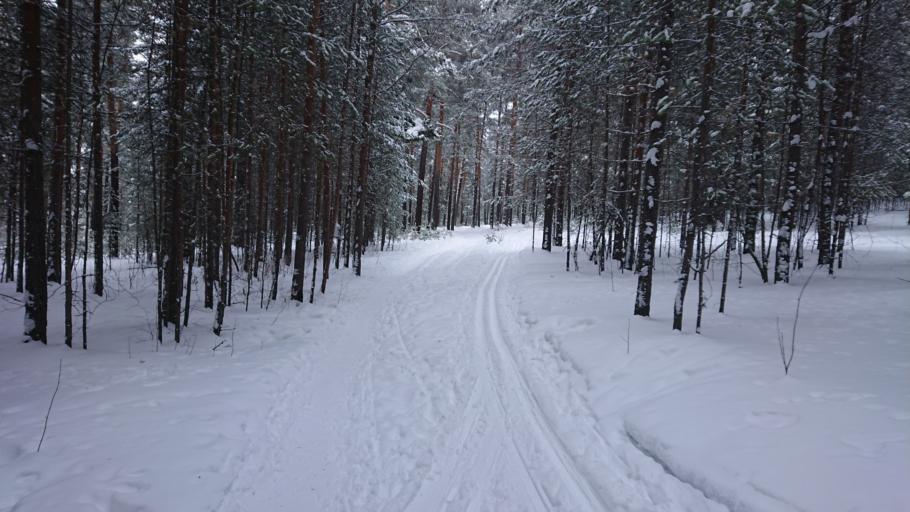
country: RU
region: Sverdlovsk
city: Degtyarsk
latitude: 56.6956
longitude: 60.0659
